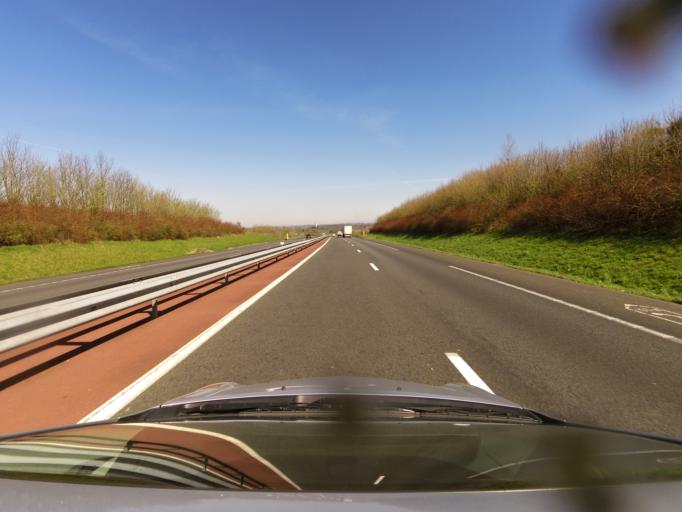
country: FR
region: Lower Normandy
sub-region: Departement de la Manche
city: Villedieu-les-Poeles
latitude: 48.7901
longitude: -1.2645
